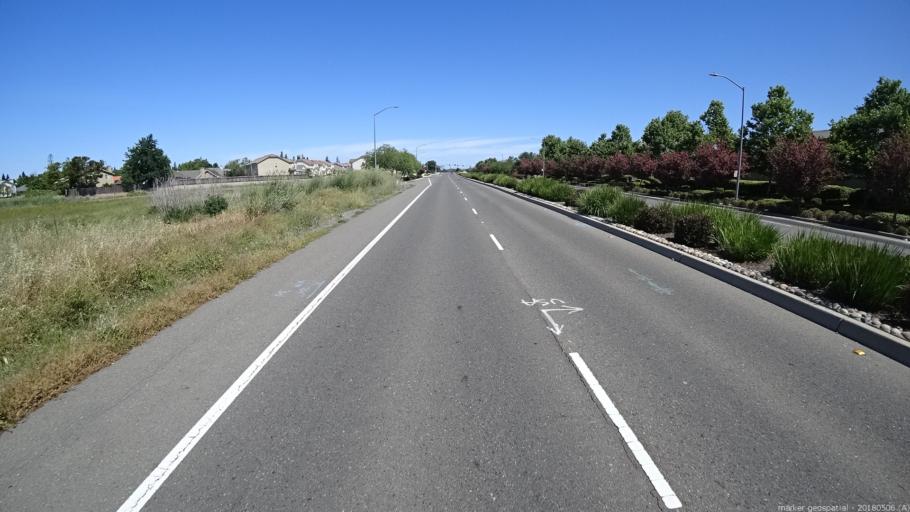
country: US
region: California
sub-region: Sacramento County
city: Laguna
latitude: 38.4407
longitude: -121.4179
